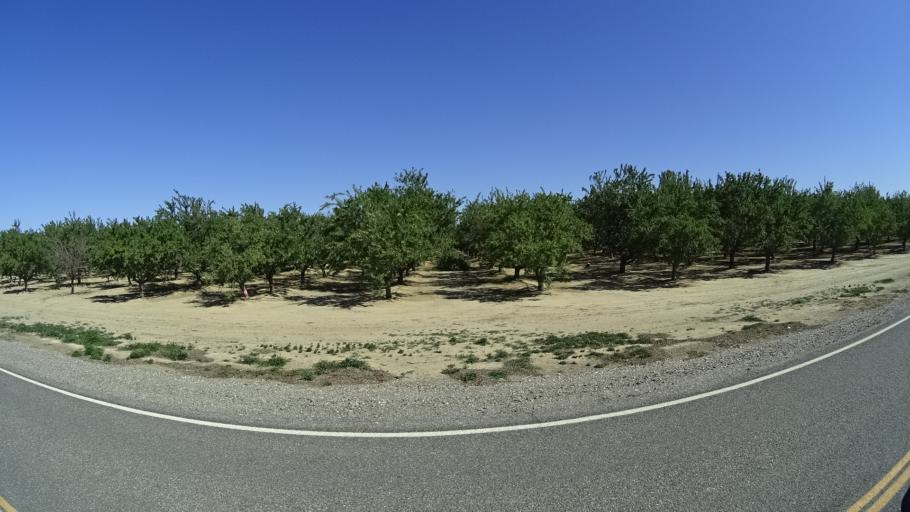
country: US
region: California
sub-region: Glenn County
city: Willows
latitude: 39.6237
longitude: -122.1400
